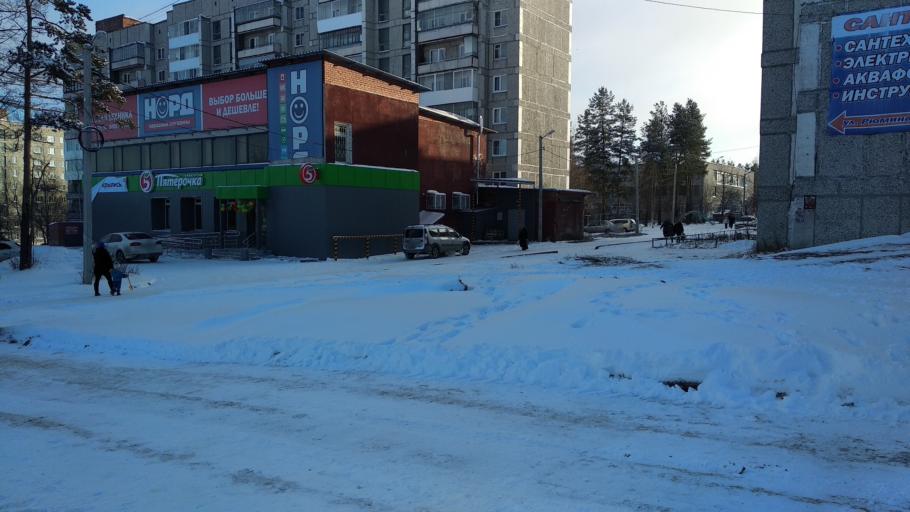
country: RU
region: Sverdlovsk
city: Krasnotur'insk
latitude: 59.7588
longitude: 60.1668
